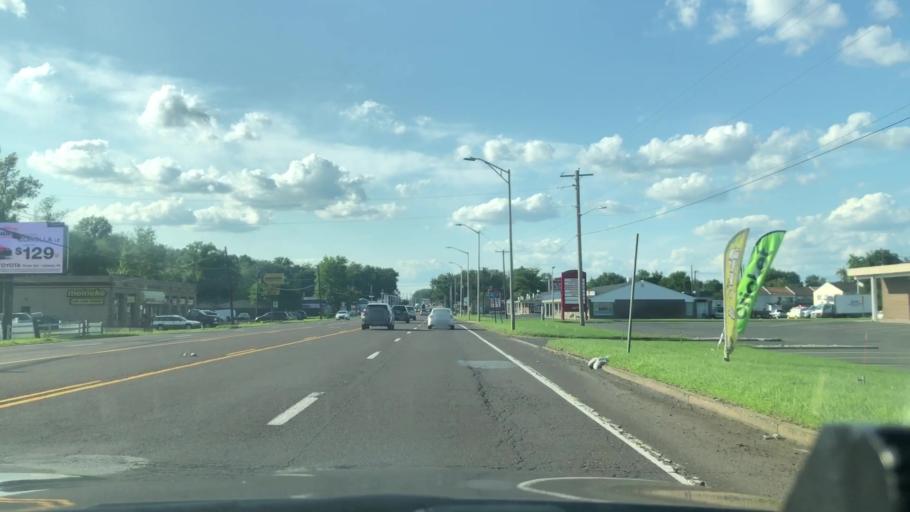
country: US
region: Pennsylvania
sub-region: Bucks County
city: Quakertown
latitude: 40.4269
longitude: -75.3486
